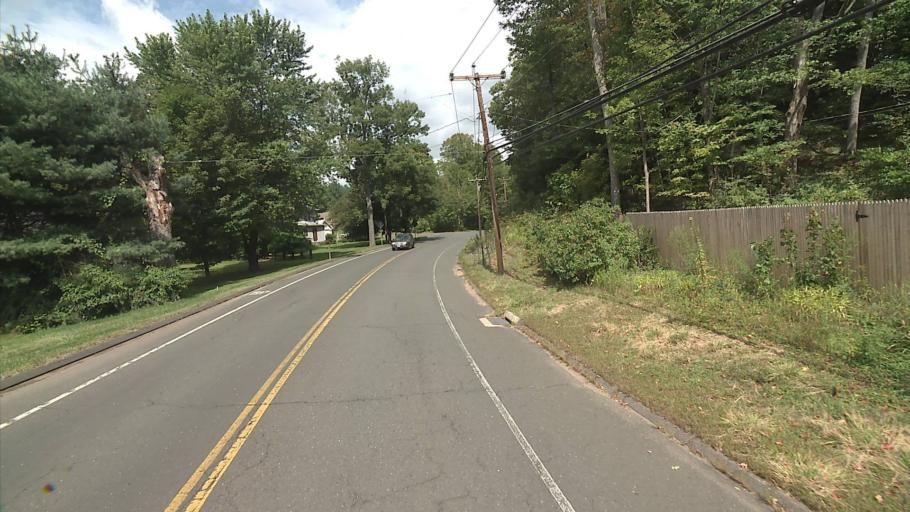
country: US
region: Connecticut
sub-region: Hartford County
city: Salmon Brook
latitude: 41.9626
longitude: -72.8014
